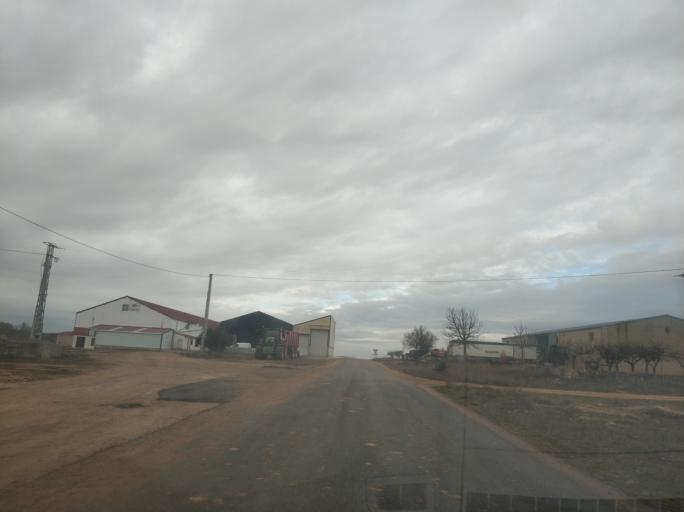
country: ES
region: Castille and Leon
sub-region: Provincia de Soria
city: Alcubilla de Avellaneda
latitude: 41.7239
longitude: -3.3091
